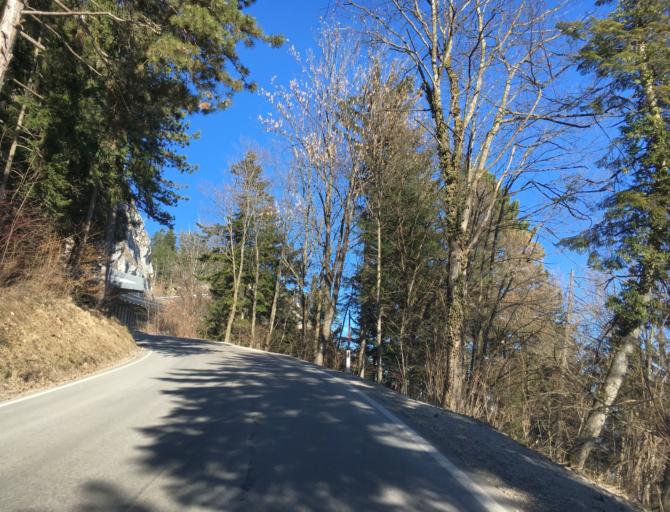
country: AT
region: Lower Austria
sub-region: Politischer Bezirk Wiener Neustadt
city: Waldegg
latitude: 47.8340
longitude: 16.0573
